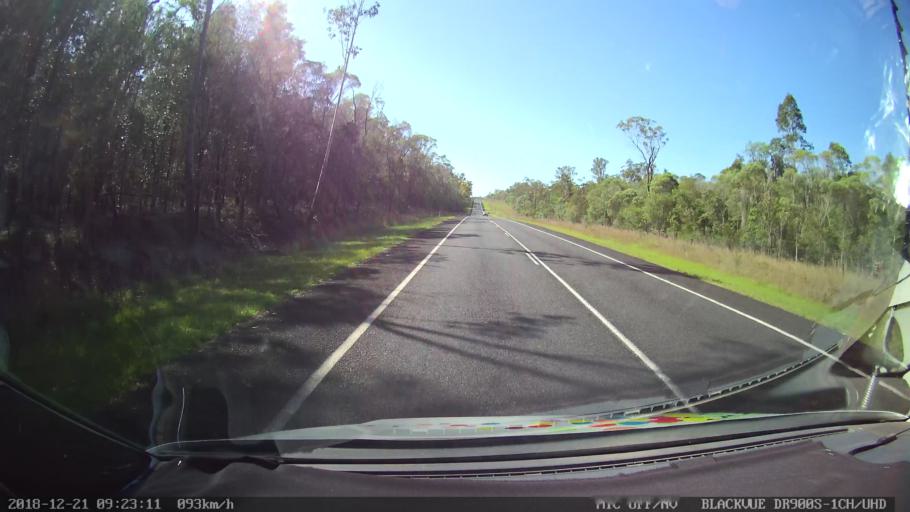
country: AU
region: New South Wales
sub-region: Clarence Valley
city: Maclean
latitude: -29.3514
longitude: 153.0111
